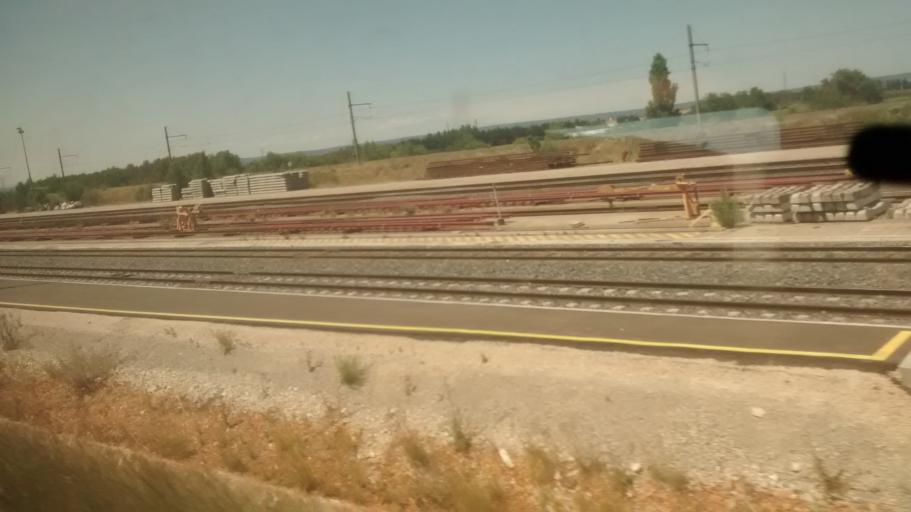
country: FR
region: Languedoc-Roussillon
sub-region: Departement du Gard
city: Redessan
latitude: 43.8191
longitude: 4.5062
